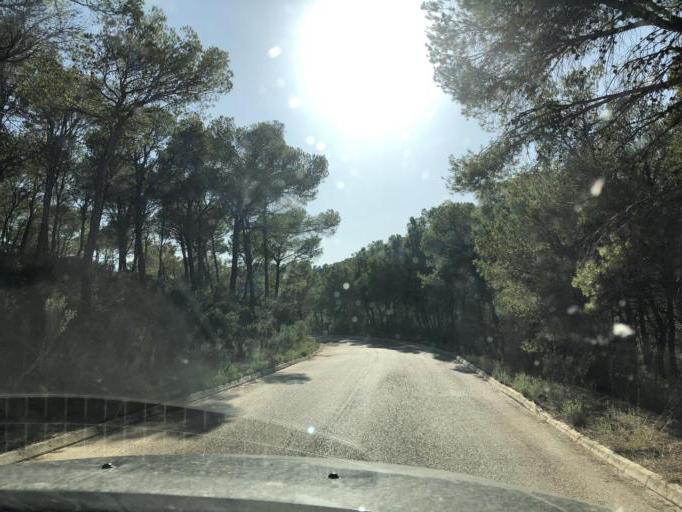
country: ES
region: Balearic Islands
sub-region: Illes Balears
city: Camp de Mar
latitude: 39.5412
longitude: 2.4068
